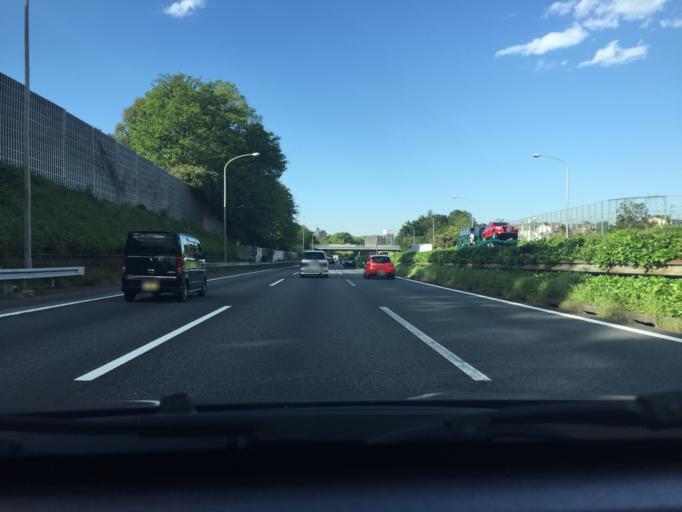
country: JP
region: Kanagawa
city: Minami-rinkan
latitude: 35.4626
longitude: 139.4331
